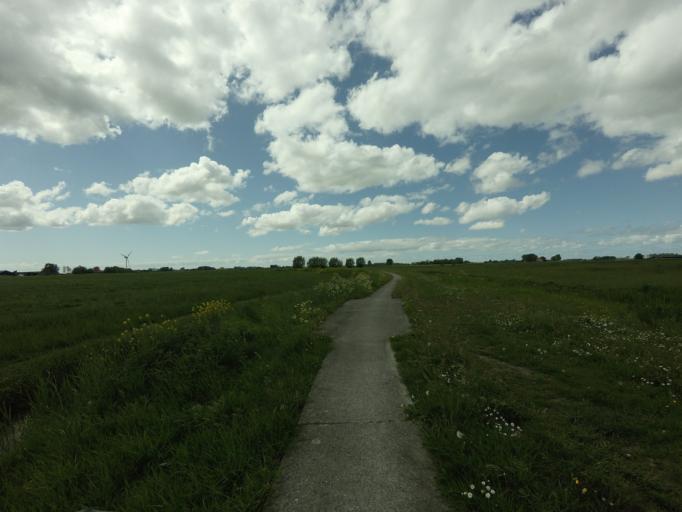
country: NL
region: Friesland
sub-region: Gemeente Littenseradiel
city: Wommels
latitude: 53.1296
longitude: 5.5680
